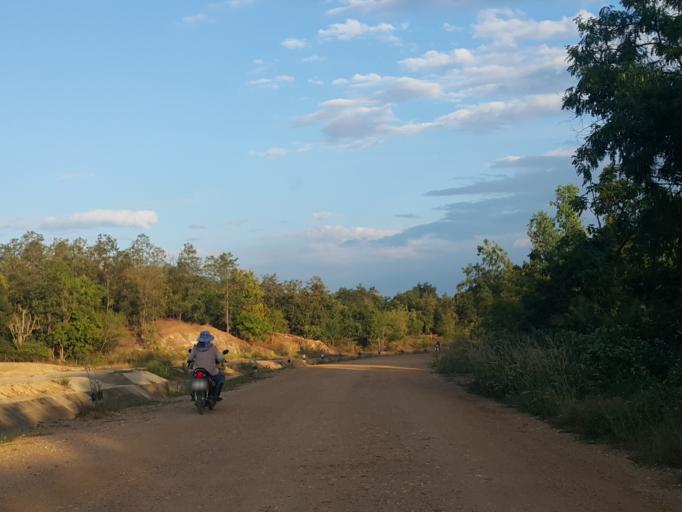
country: TH
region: Lampang
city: Mae Mo
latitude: 18.4340
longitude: 99.5994
